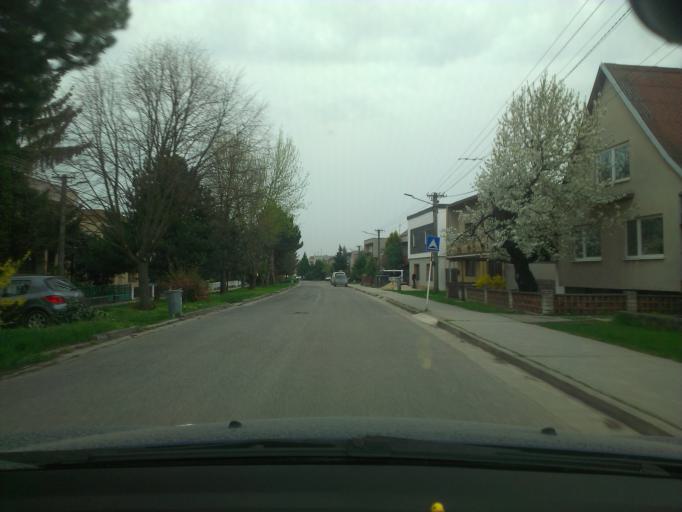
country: SK
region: Trnavsky
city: Vrbove
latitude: 48.6175
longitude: 17.7250
